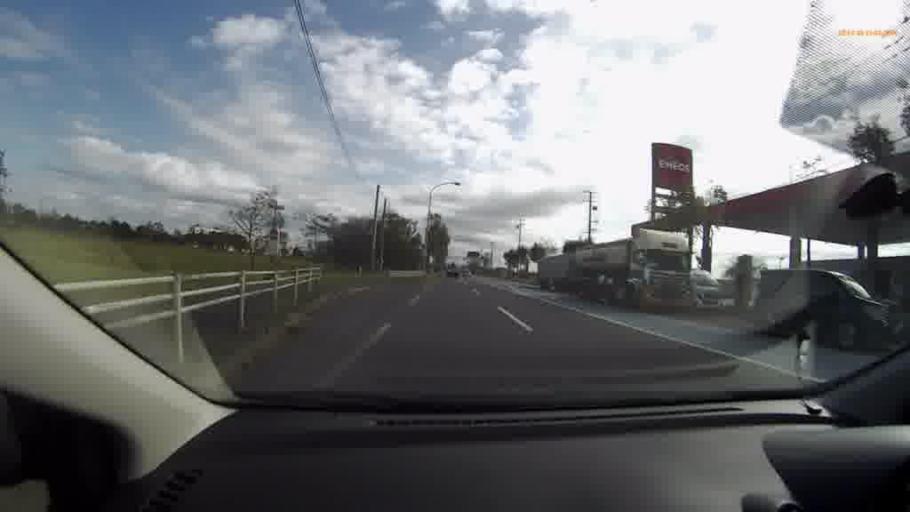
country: JP
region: Hokkaido
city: Kushiro
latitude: 43.0102
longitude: 144.2874
